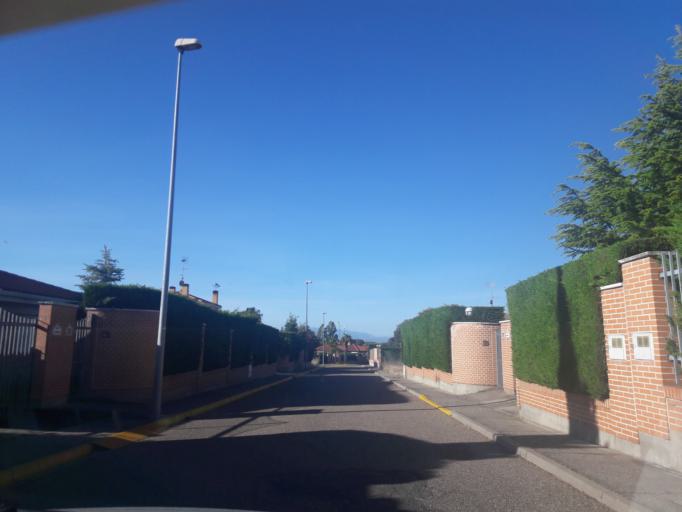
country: ES
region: Castille and Leon
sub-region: Provincia de Salamanca
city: Martinamor
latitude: 40.8057
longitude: -5.6338
